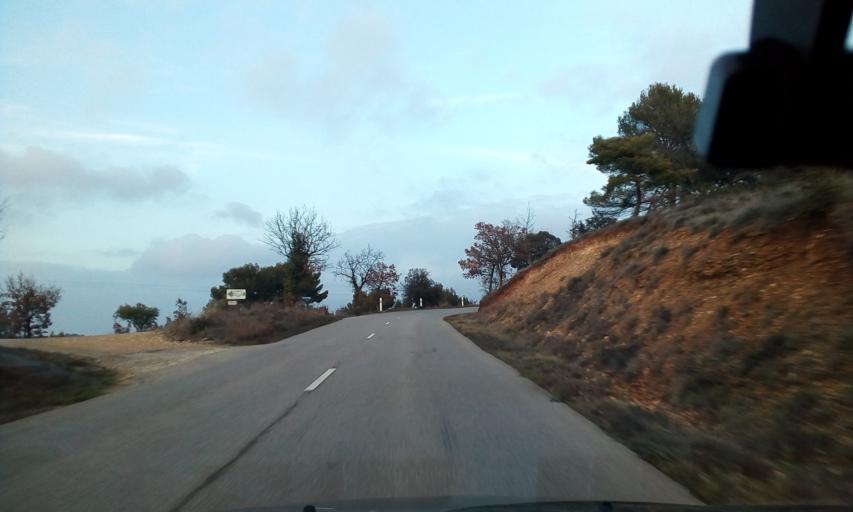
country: FR
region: Provence-Alpes-Cote d'Azur
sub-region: Departement des Alpes-de-Haute-Provence
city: Greoux-les-Bains
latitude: 43.7896
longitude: 5.8617
